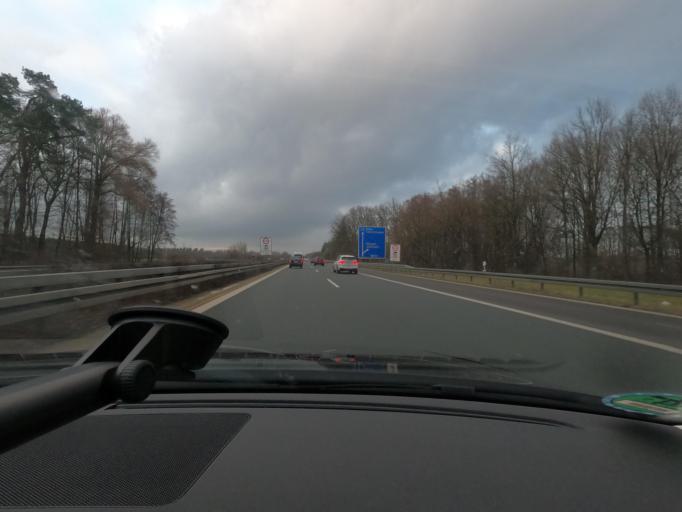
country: DE
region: Bavaria
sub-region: Regierungsbezirk Mittelfranken
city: Erlangen
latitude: 49.5353
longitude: 10.9927
